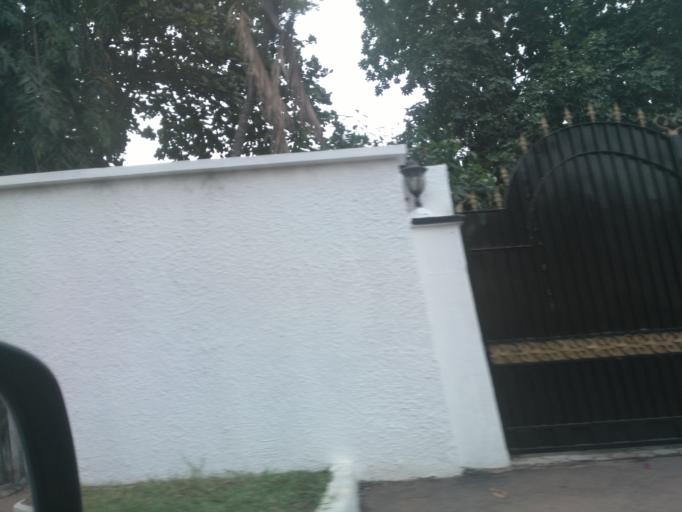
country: GH
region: Greater Accra
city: Accra
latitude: 5.6057
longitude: -0.1849
